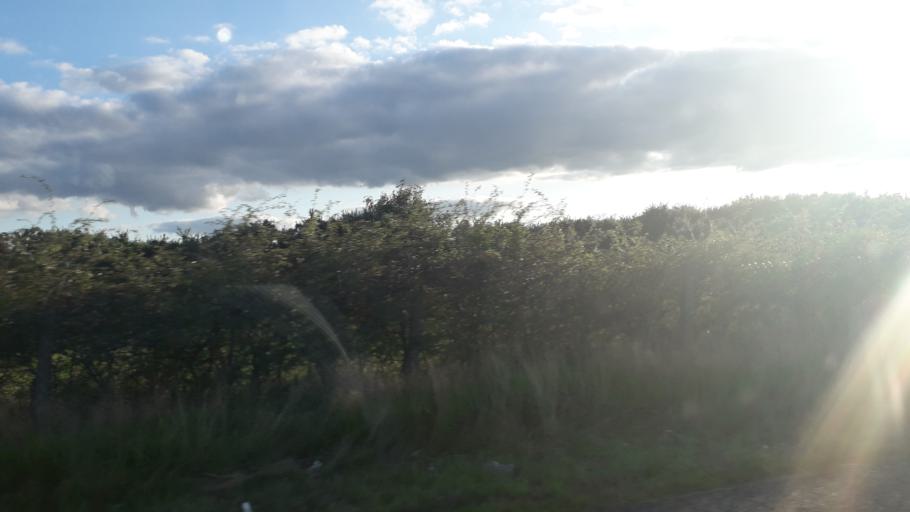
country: IE
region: Leinster
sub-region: Lu
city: Blackrock
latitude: 54.0113
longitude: -6.3035
